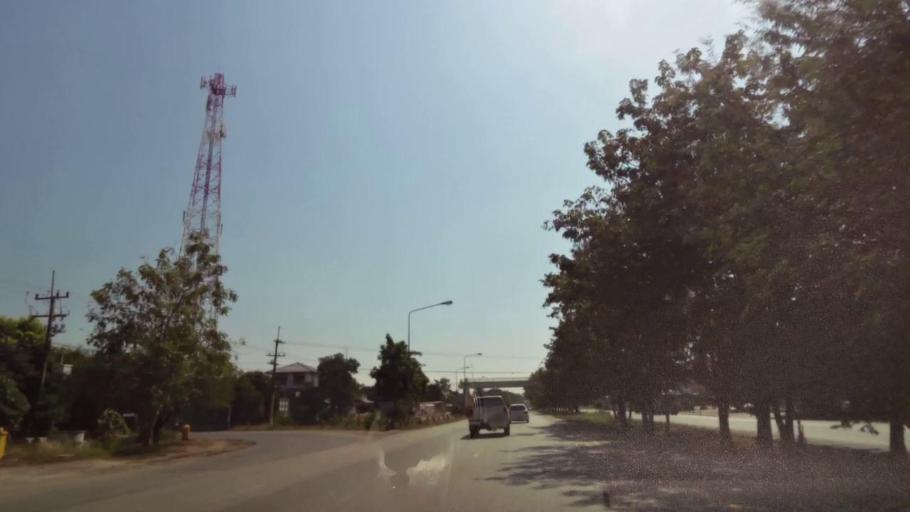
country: TH
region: Nakhon Sawan
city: Kao Liao
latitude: 15.8705
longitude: 100.1165
